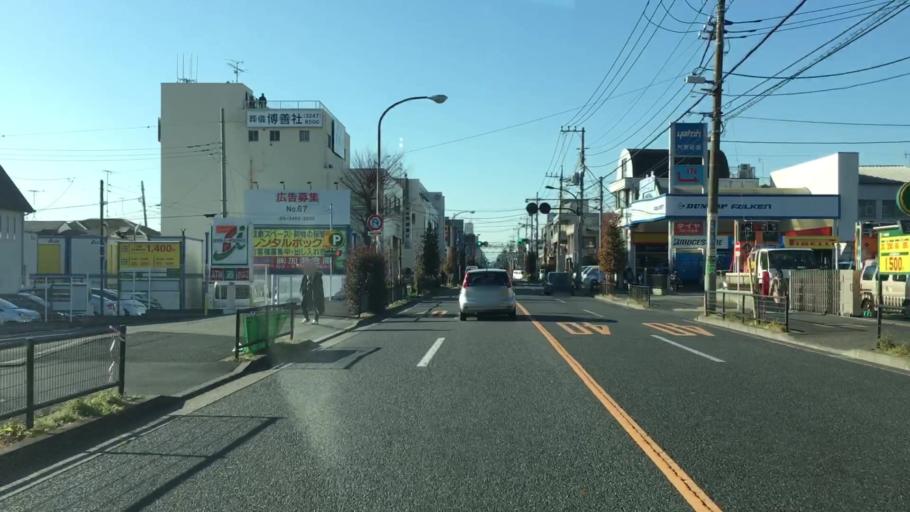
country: JP
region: Tokyo
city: Mitaka-shi
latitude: 35.6932
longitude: 139.6040
